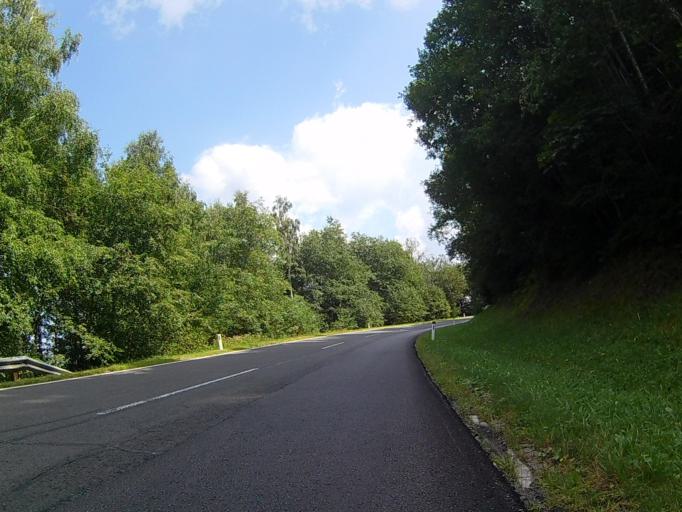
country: AT
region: Styria
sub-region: Politischer Bezirk Deutschlandsberg
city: Soboth
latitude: 46.6958
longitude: 15.1004
